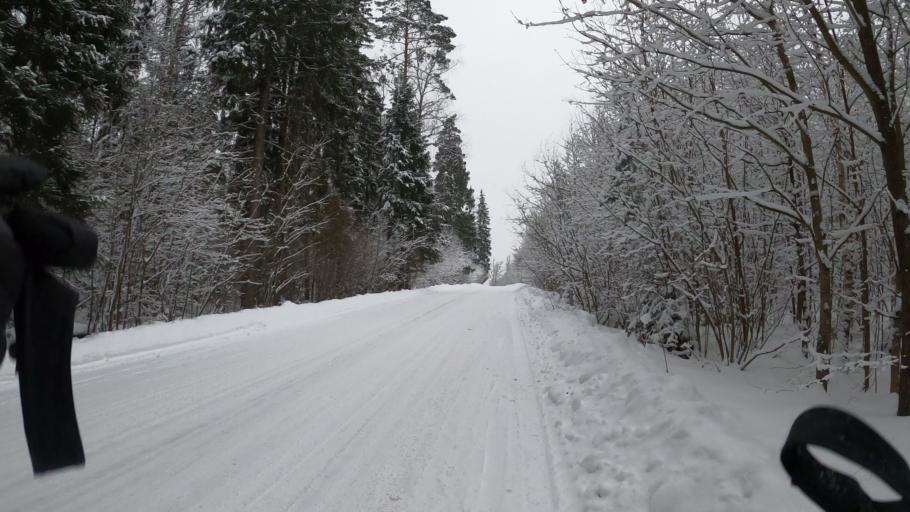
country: RU
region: Moskovskaya
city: Firsanovka
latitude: 55.9226
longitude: 37.2134
